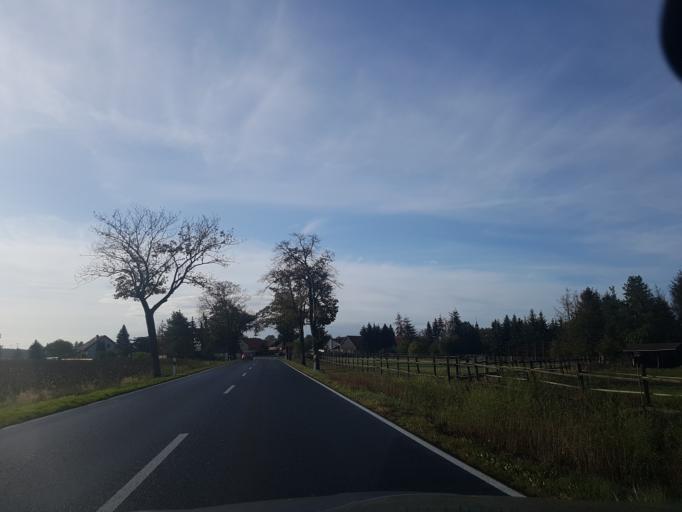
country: DE
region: Saxony
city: Arzberg
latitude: 51.6173
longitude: 13.1466
